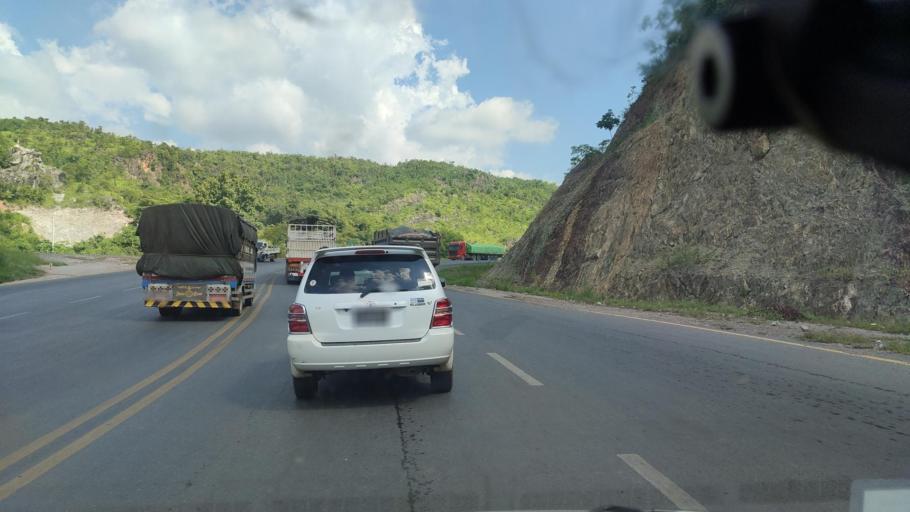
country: MM
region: Mandalay
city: Mandalay
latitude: 21.8518
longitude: 96.2654
